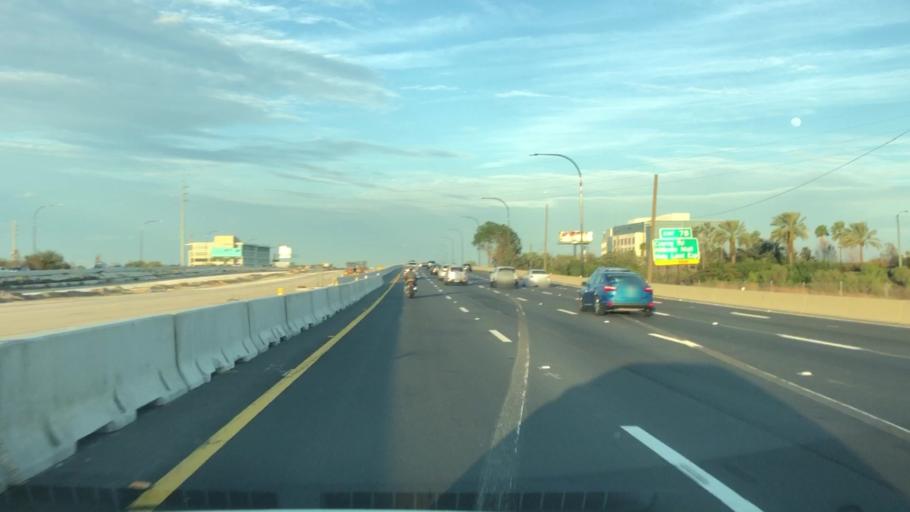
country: US
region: Florida
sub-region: Orange County
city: Oak Ridge
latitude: 28.4830
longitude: -81.4438
